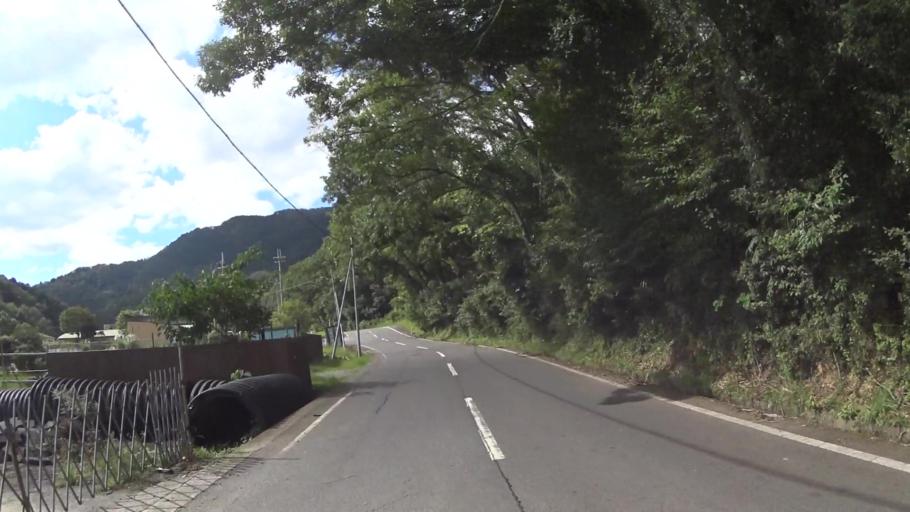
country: JP
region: Shiga Prefecture
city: Otsu-shi
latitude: 34.9487
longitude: 135.8884
